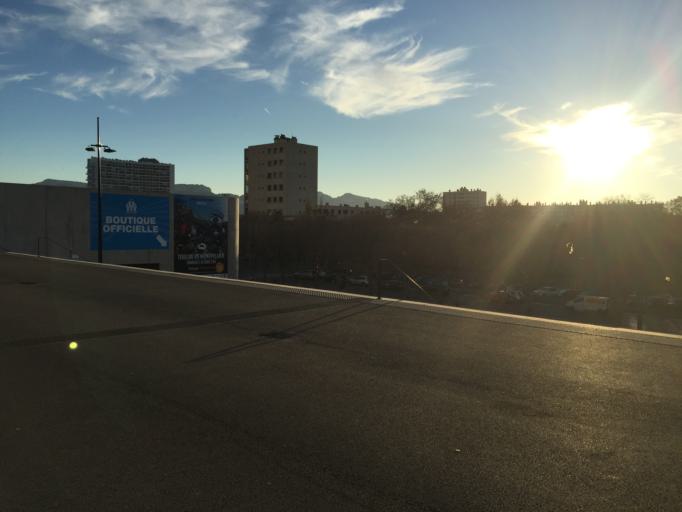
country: FR
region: Provence-Alpes-Cote d'Azur
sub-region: Departement des Bouches-du-Rhone
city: Marseille 08
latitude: 43.2693
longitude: 5.3941
